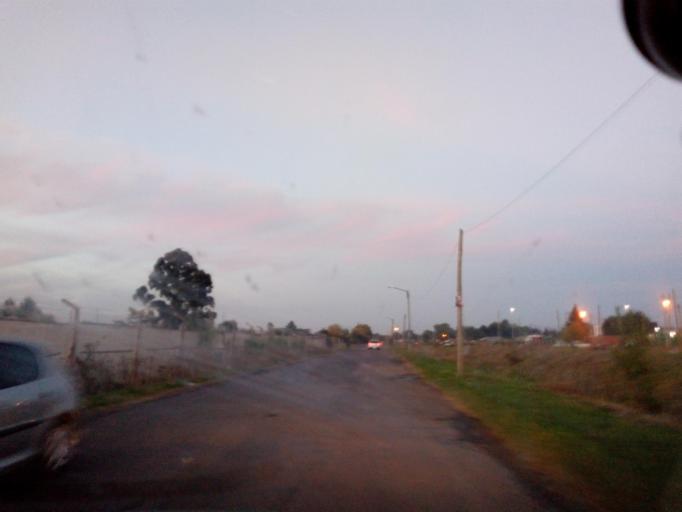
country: AR
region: Buenos Aires
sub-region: Partido de La Plata
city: La Plata
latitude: -34.9961
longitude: -58.0368
